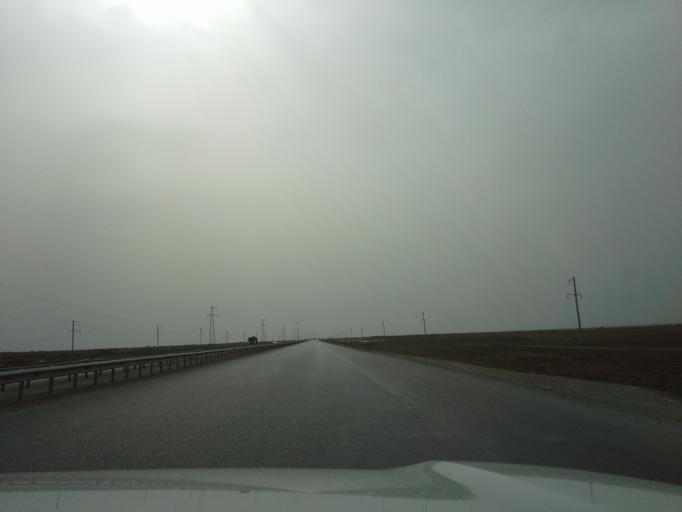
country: TM
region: Ahal
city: Kaka
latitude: 37.5417
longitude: 59.3982
